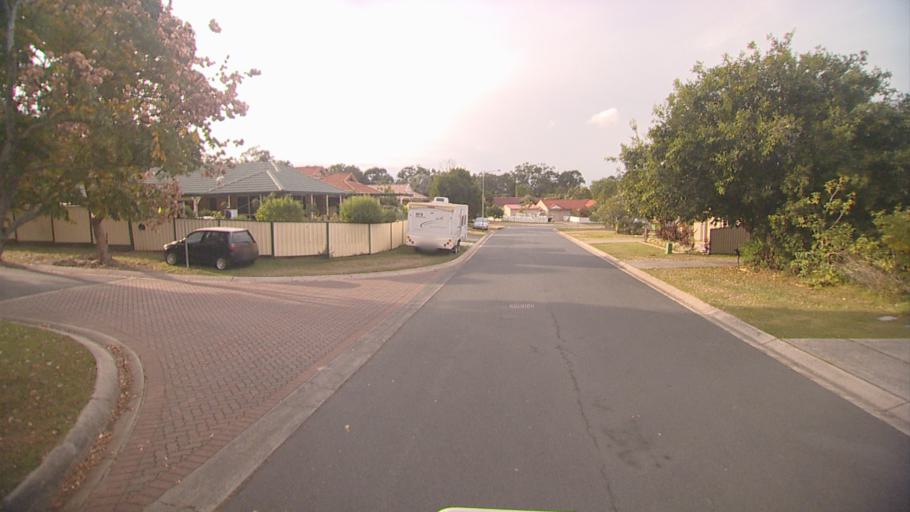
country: AU
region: Queensland
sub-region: Logan
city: Park Ridge South
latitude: -27.6752
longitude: 153.0199
